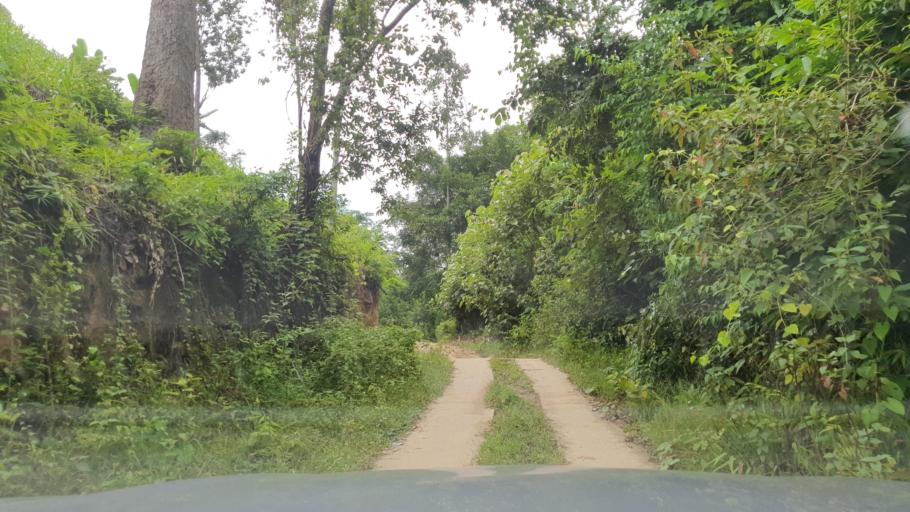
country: TH
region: Chiang Mai
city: Mae Wang
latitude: 18.6622
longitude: 98.6199
